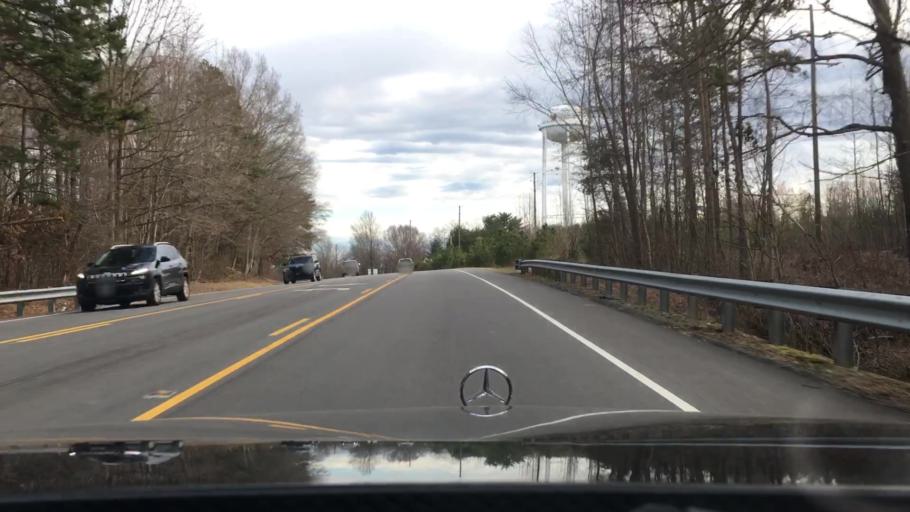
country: US
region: North Carolina
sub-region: Caswell County
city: Yanceyville
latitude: 36.4096
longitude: -79.3414
